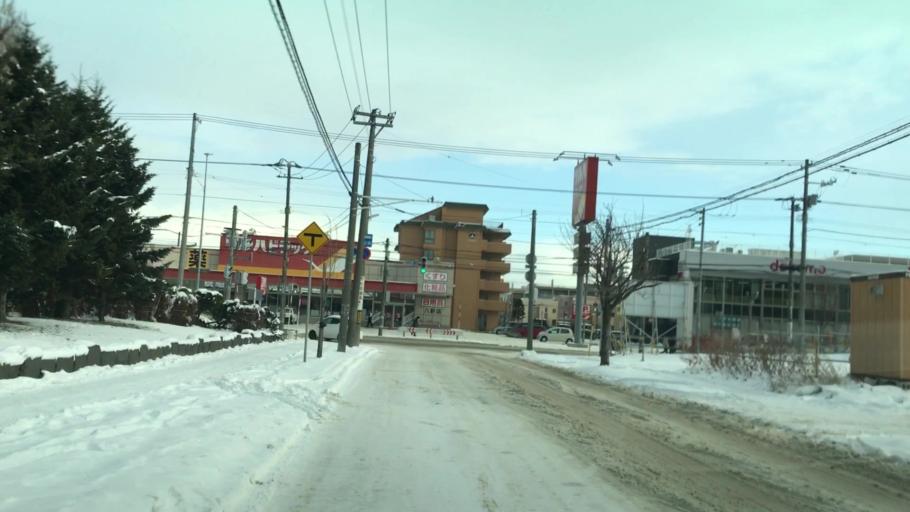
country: JP
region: Hokkaido
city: Sapporo
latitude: 43.0915
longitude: 141.3064
